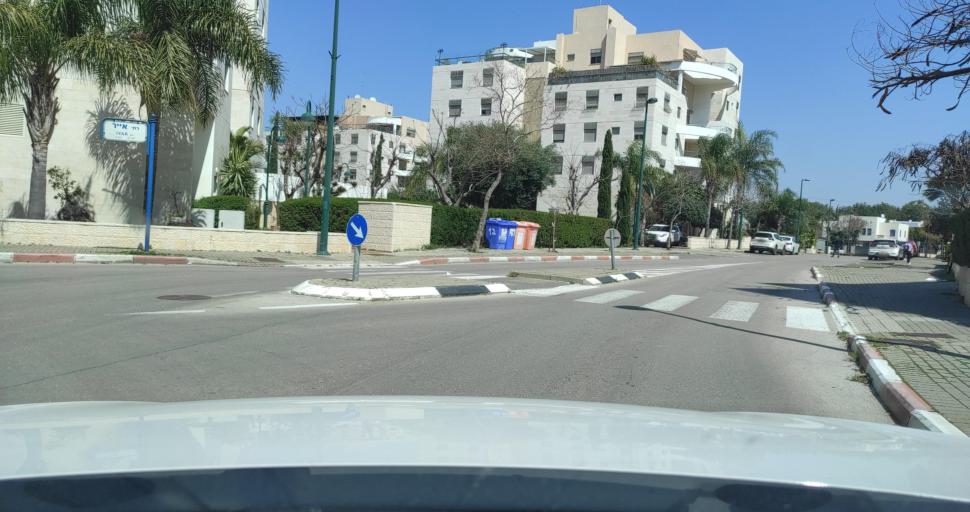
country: IL
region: Central District
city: Nordiyya
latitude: 32.2966
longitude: 34.8759
